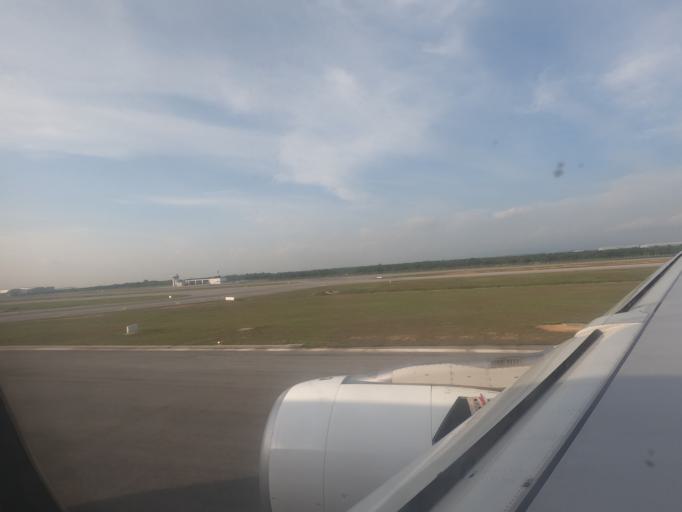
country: MY
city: Sungai Pelek New Village
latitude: 2.7198
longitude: 101.6898
